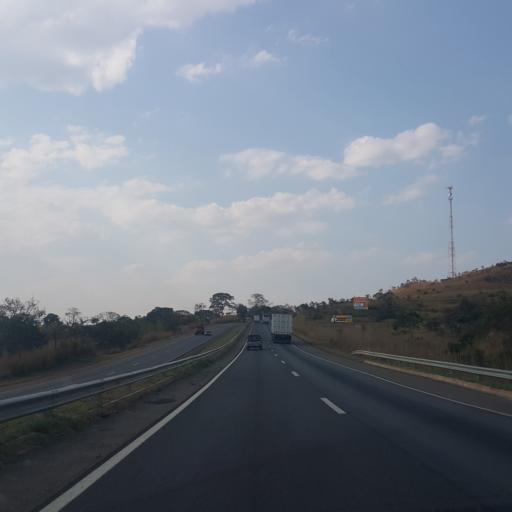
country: BR
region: Goias
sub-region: Abadiania
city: Abadiania
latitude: -16.1025
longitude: -48.5235
